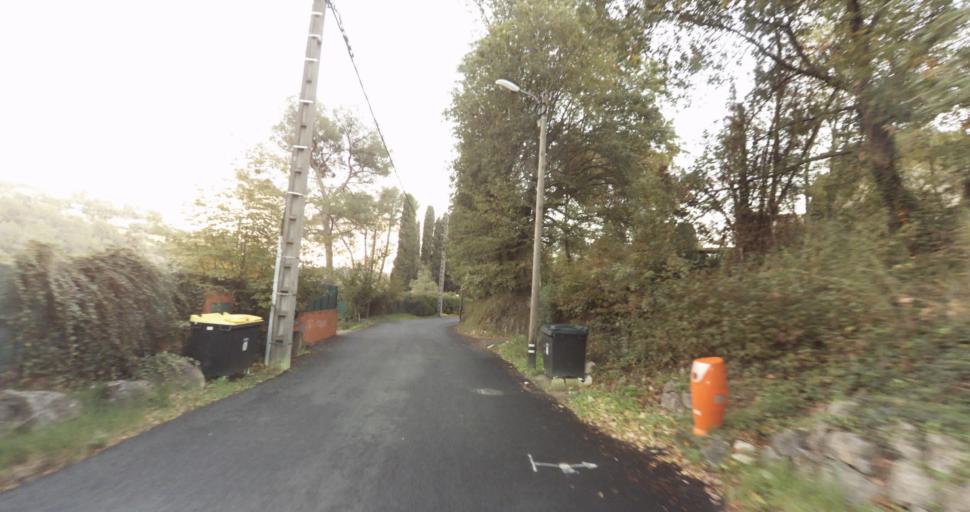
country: FR
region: Provence-Alpes-Cote d'Azur
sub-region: Departement des Alpes-Maritimes
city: Vence
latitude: 43.7228
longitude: 7.1267
